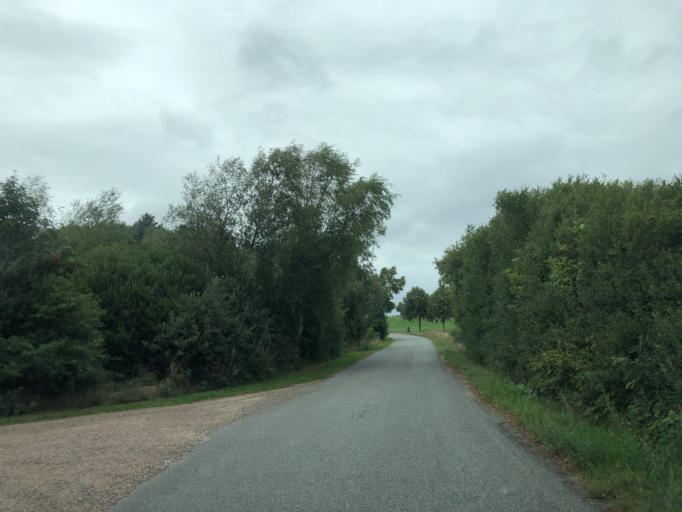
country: DK
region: Central Jutland
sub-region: Herning Kommune
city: Lind
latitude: 56.0828
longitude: 8.9562
